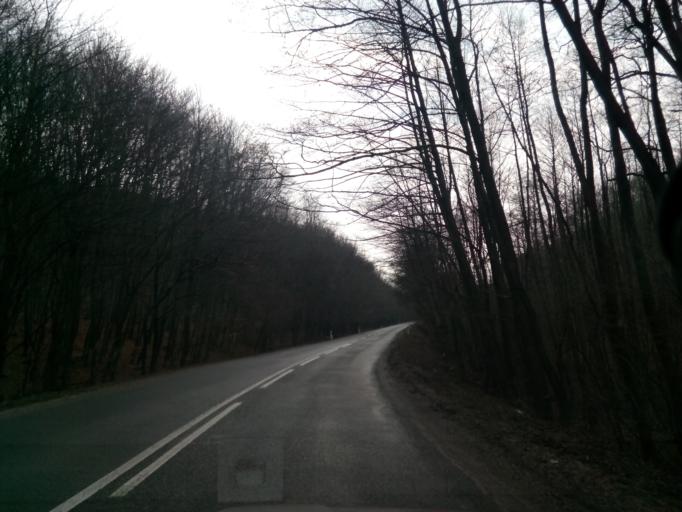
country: SK
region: Kosicky
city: Kosice
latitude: 48.6420
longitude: 21.4404
